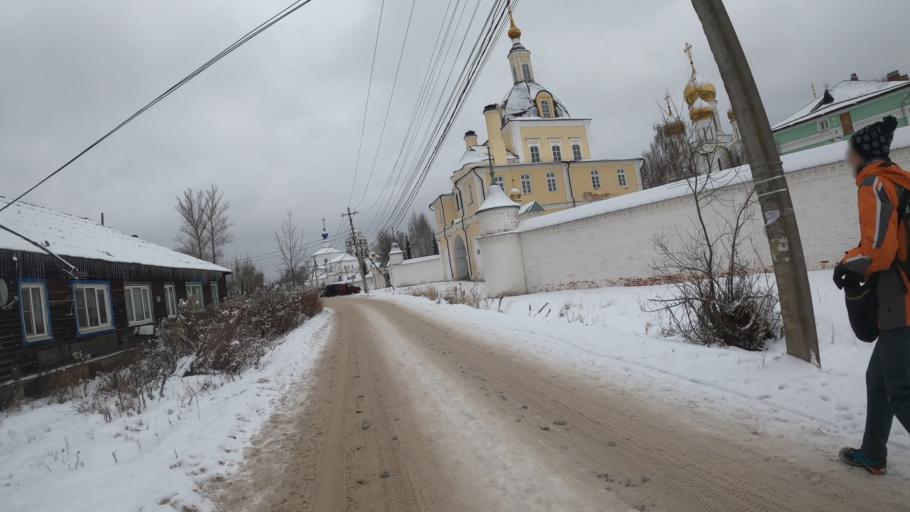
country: RU
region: Jaroslavl
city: Pereslavl'-Zalesskiy
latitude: 56.7327
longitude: 38.8388
